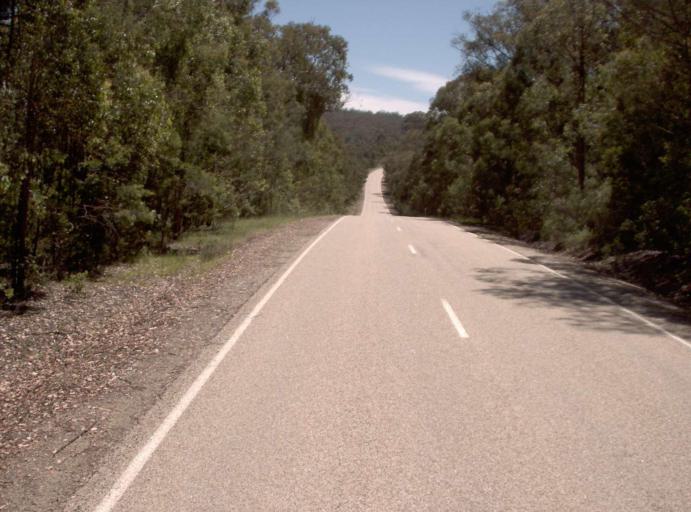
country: AU
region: Victoria
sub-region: East Gippsland
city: Lakes Entrance
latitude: -37.3294
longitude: 148.2354
